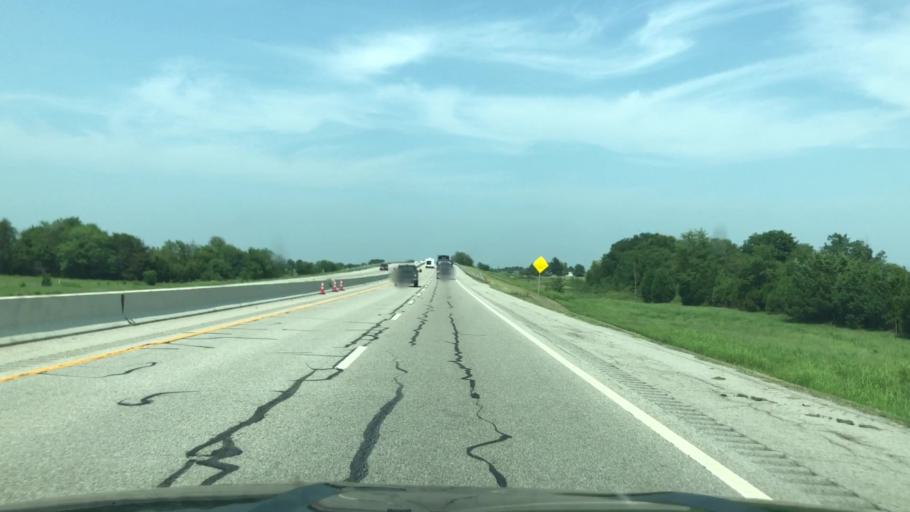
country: US
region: Oklahoma
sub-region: Ottawa County
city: Fairland
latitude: 36.8093
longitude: -94.8763
